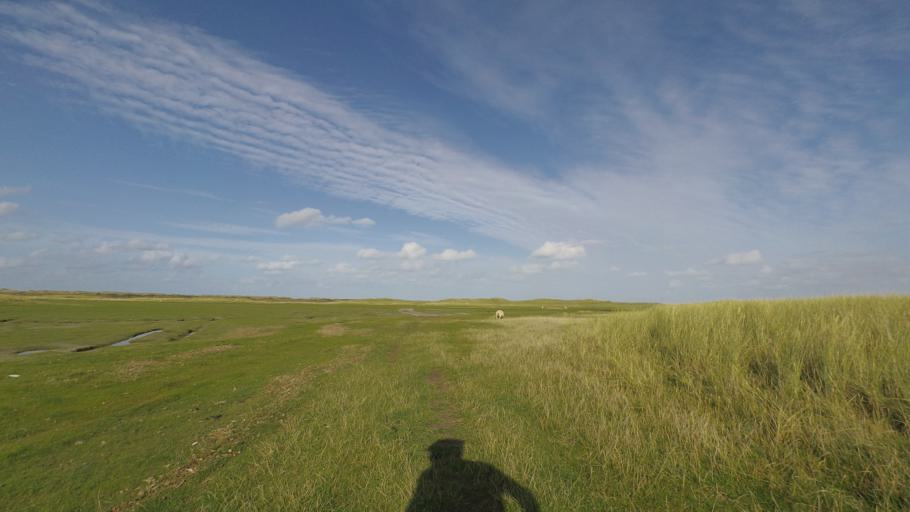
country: NL
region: Friesland
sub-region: Gemeente Ameland
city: Nes
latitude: 53.4537
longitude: 5.8622
